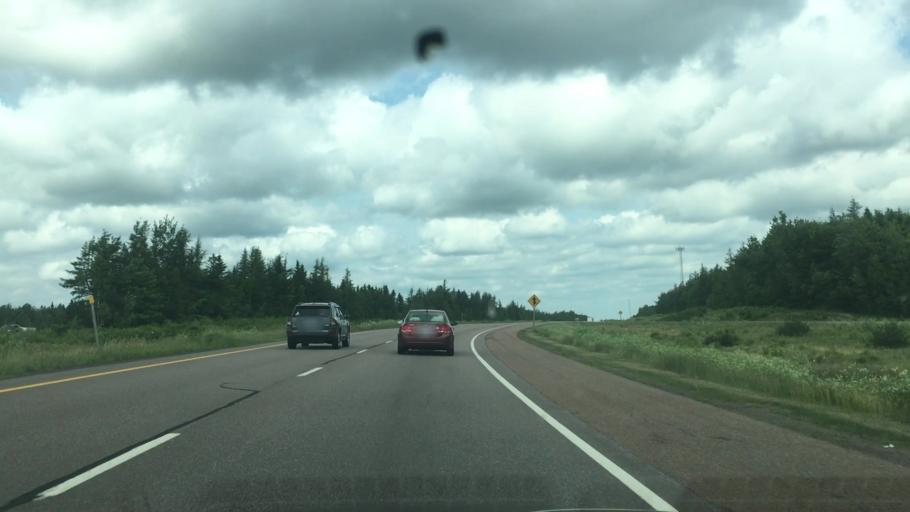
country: CA
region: New Brunswick
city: Dieppe
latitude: 46.0517
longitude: -64.5854
